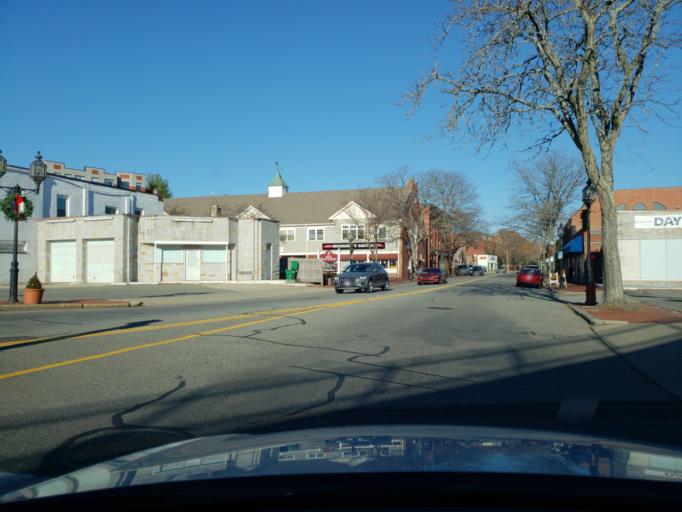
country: US
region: Massachusetts
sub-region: Middlesex County
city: Winchester
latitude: 42.4530
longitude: -71.1372
